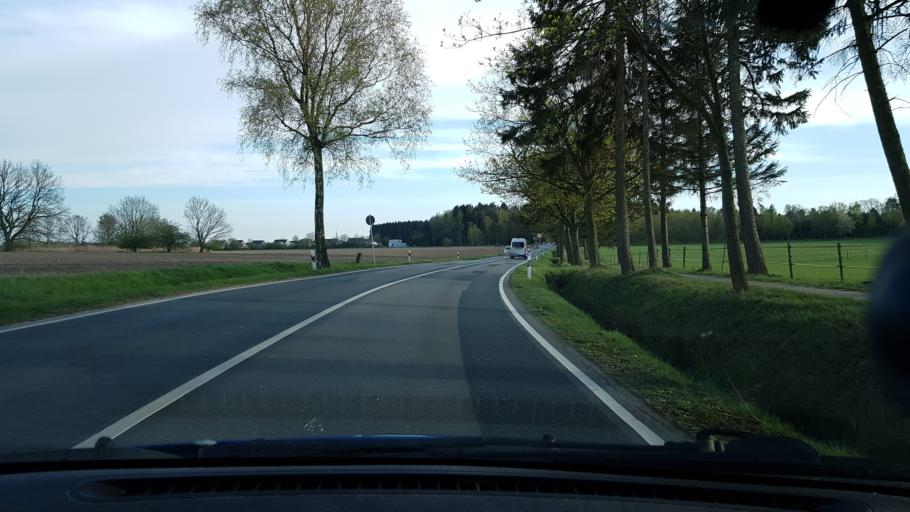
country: DE
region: Lower Saxony
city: Buchholz in der Nordheide
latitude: 53.3485
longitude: 9.8822
